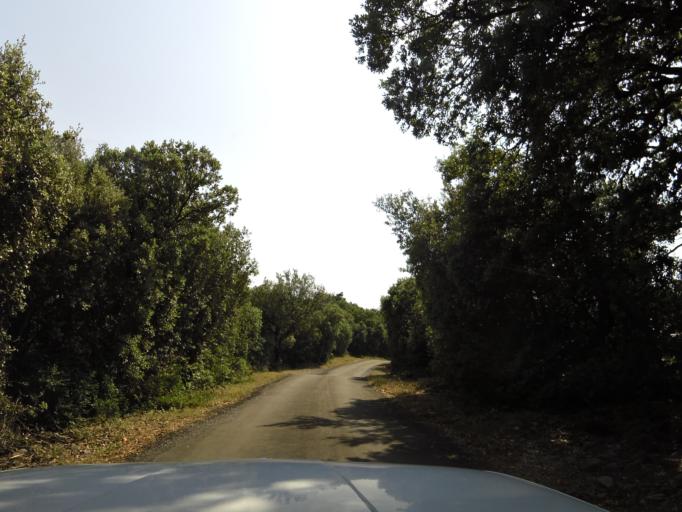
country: FR
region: Languedoc-Roussillon
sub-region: Departement du Gard
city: Anduze
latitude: 44.1078
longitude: 3.9633
